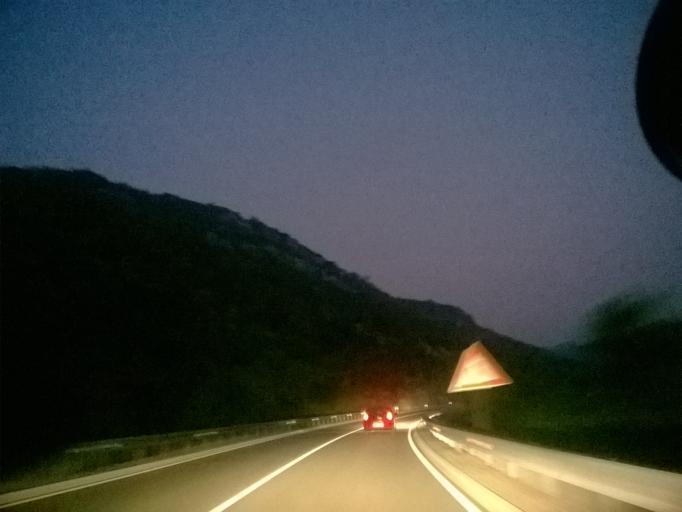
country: ME
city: Mojanovici
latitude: 42.3856
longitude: 19.0891
